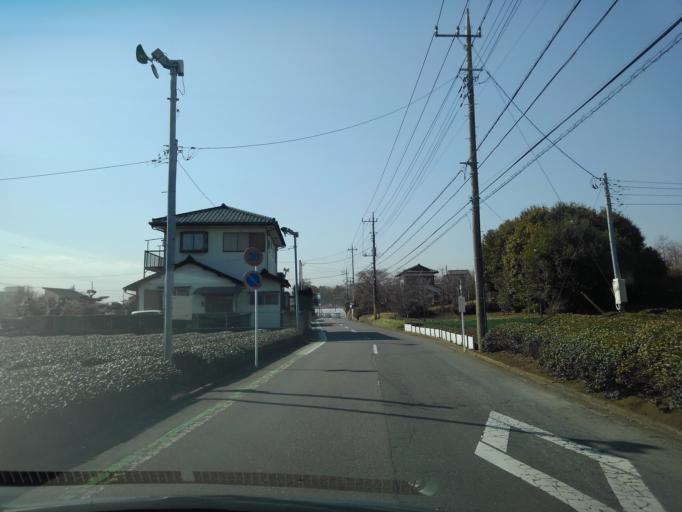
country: JP
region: Saitama
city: Tokorozawa
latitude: 35.7967
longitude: 139.4947
